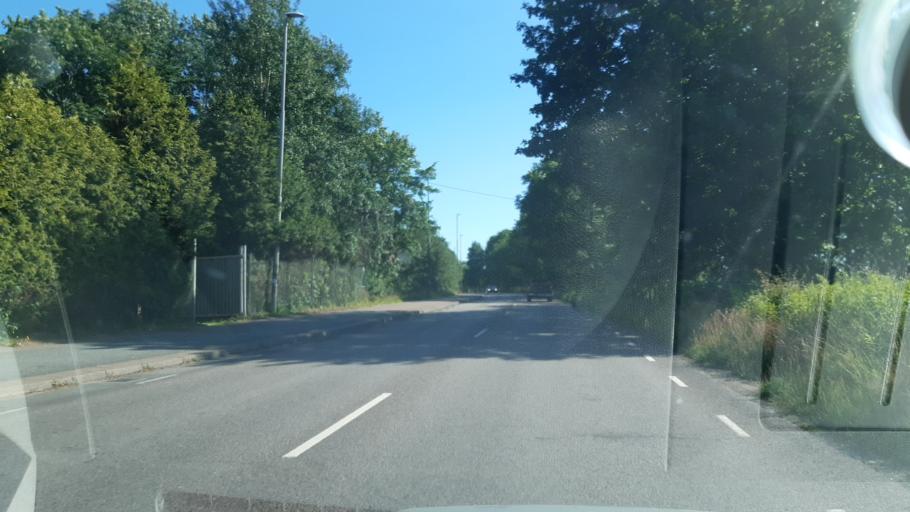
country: SE
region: Vaestra Goetaland
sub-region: Goteborg
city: Eriksbo
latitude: 57.7413
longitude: 12.0066
